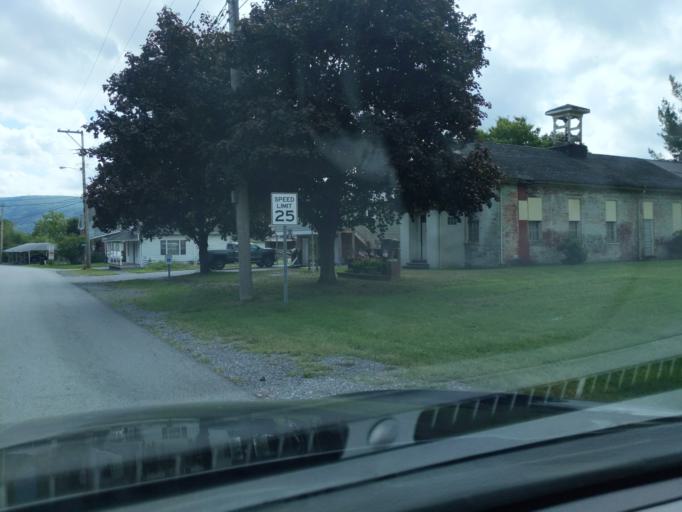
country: US
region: Pennsylvania
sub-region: Blair County
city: Duncansville
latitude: 40.3937
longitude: -78.4336
